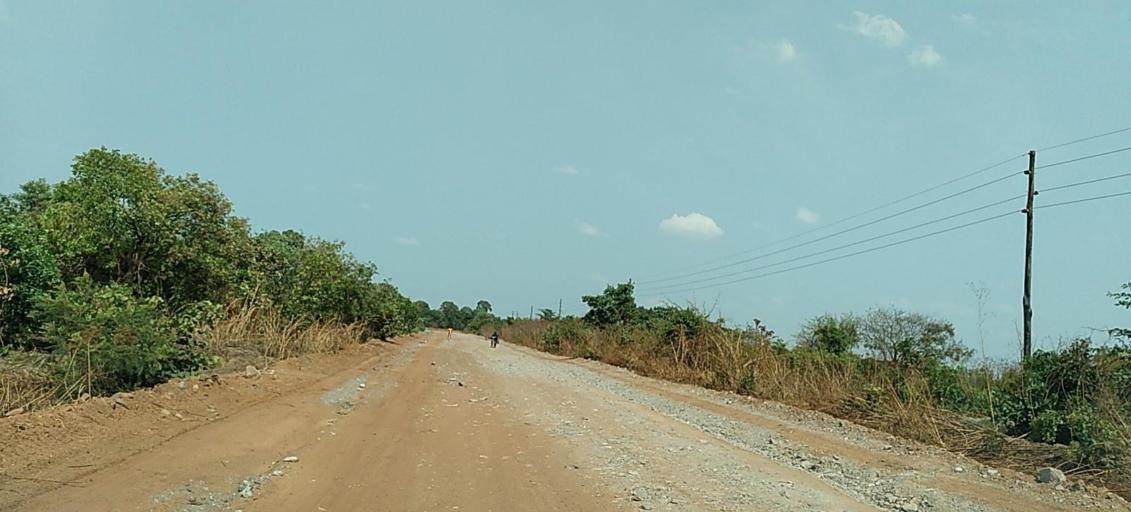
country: ZM
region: Copperbelt
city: Luanshya
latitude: -13.0936
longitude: 28.3118
